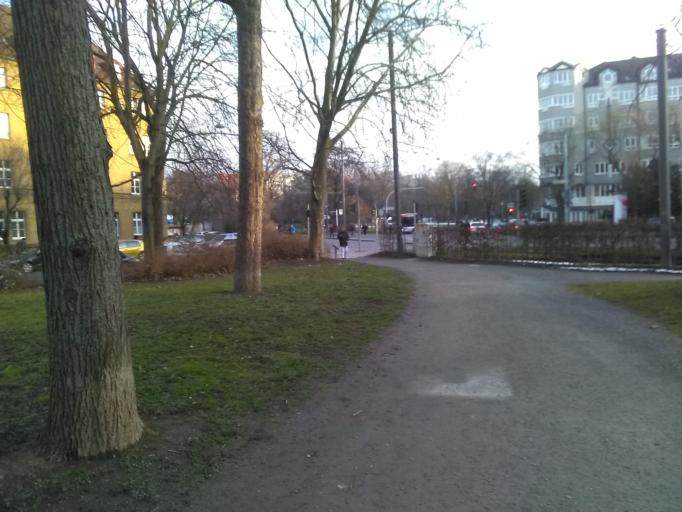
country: DE
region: Bavaria
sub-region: Regierungsbezirk Unterfranken
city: Wuerzburg
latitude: 49.7999
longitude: 9.9408
